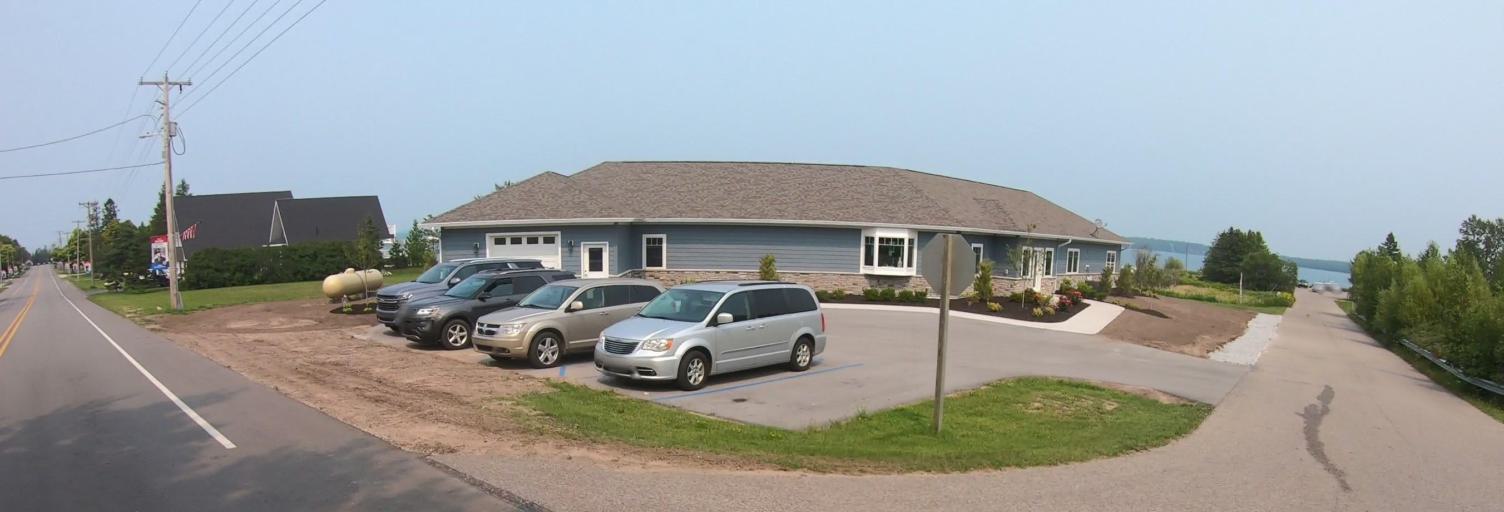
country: CA
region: Ontario
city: Thessalon
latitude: 45.9939
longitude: -83.9016
